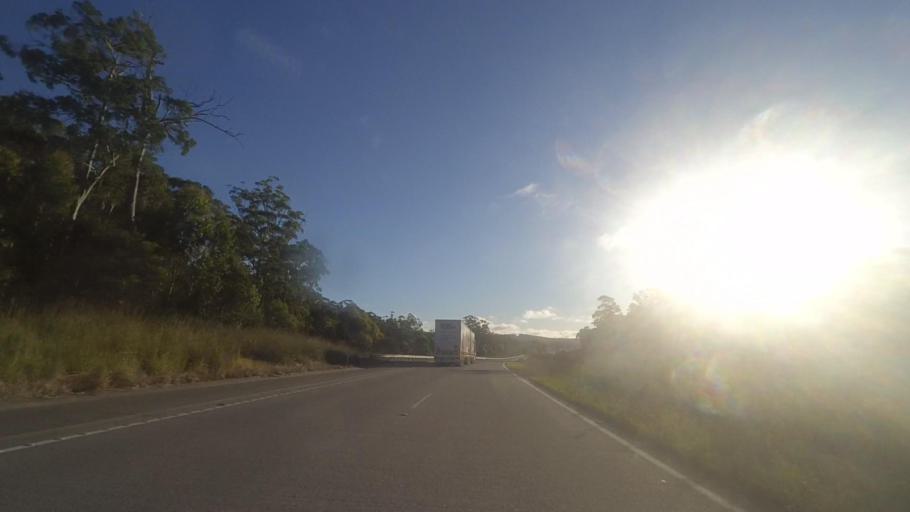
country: AU
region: New South Wales
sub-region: Great Lakes
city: Bulahdelah
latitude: -32.5170
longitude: 152.2083
